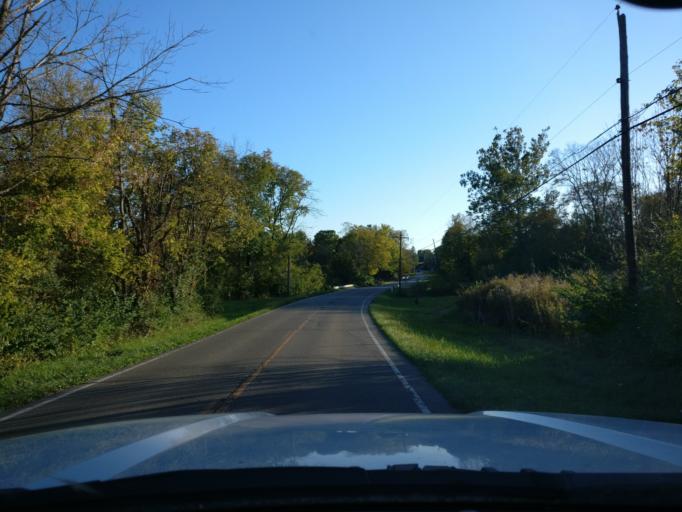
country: US
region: Ohio
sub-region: Warren County
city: Hunter
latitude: 39.4995
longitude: -84.2779
